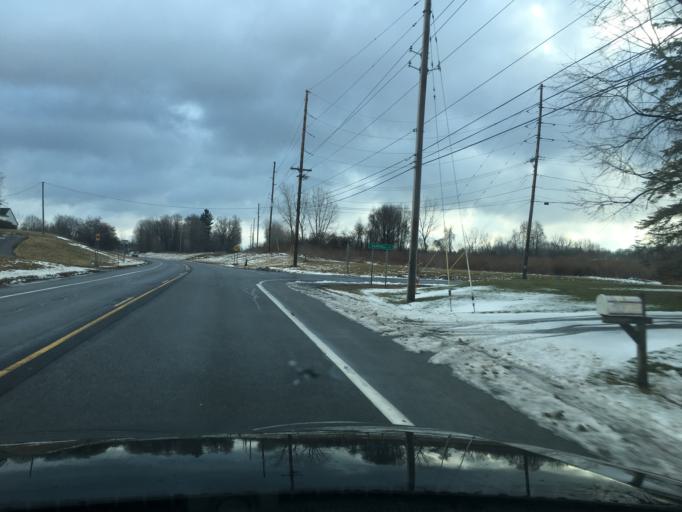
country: US
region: New York
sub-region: Ontario County
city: Manchester
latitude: 42.9670
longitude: -77.2626
